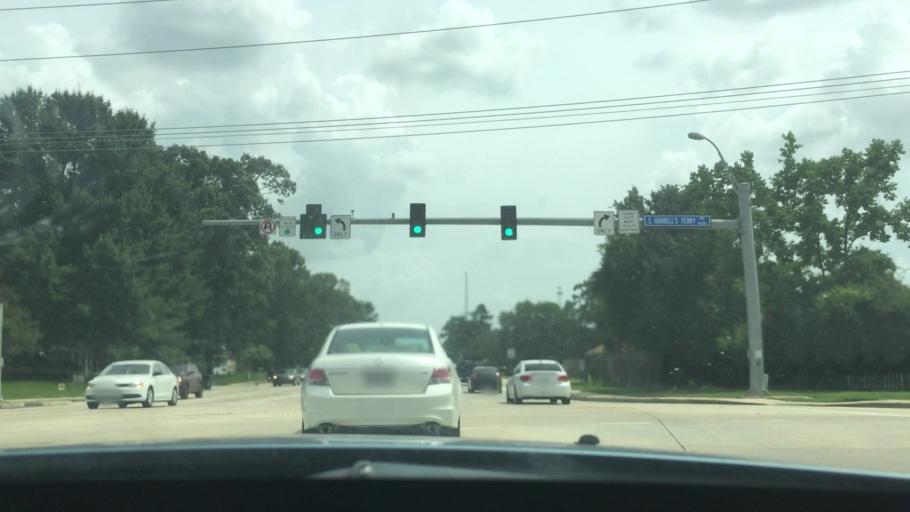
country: US
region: Louisiana
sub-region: East Baton Rouge Parish
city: Shenandoah
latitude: 30.4255
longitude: -91.0076
